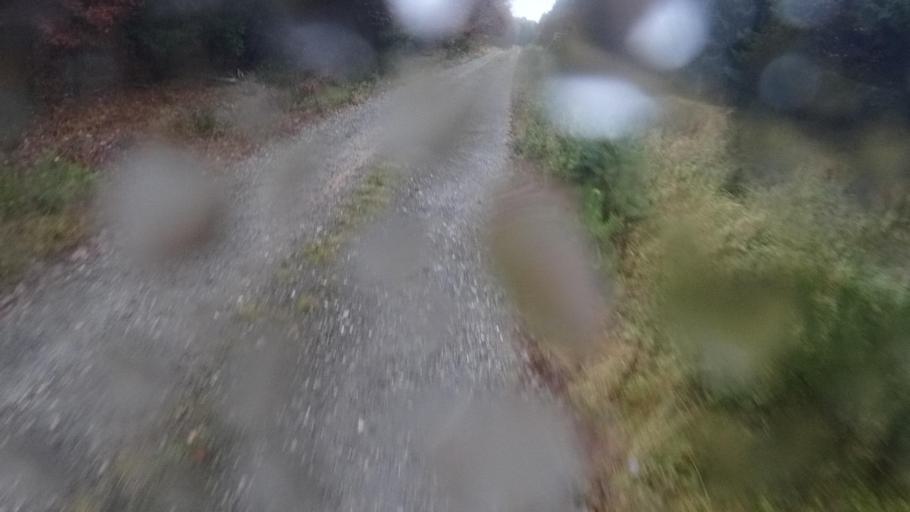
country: DE
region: Rheinland-Pfalz
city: Wiebelsheim
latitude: 50.0987
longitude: 7.6280
